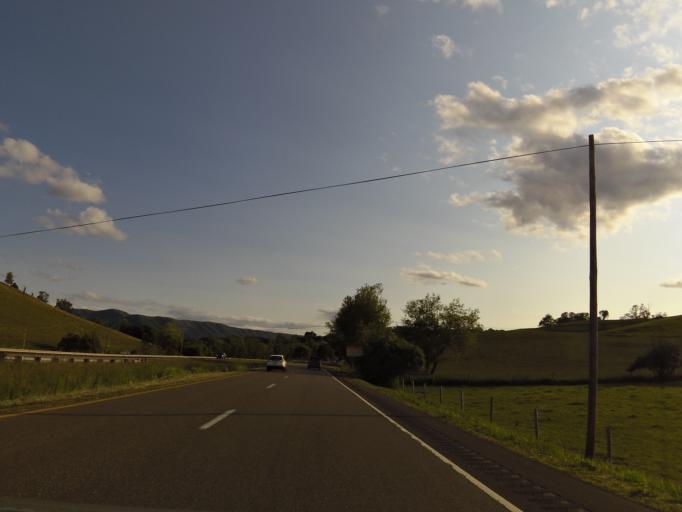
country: US
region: Virginia
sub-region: Russell County
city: Honaker
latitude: 36.9407
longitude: -81.9627
